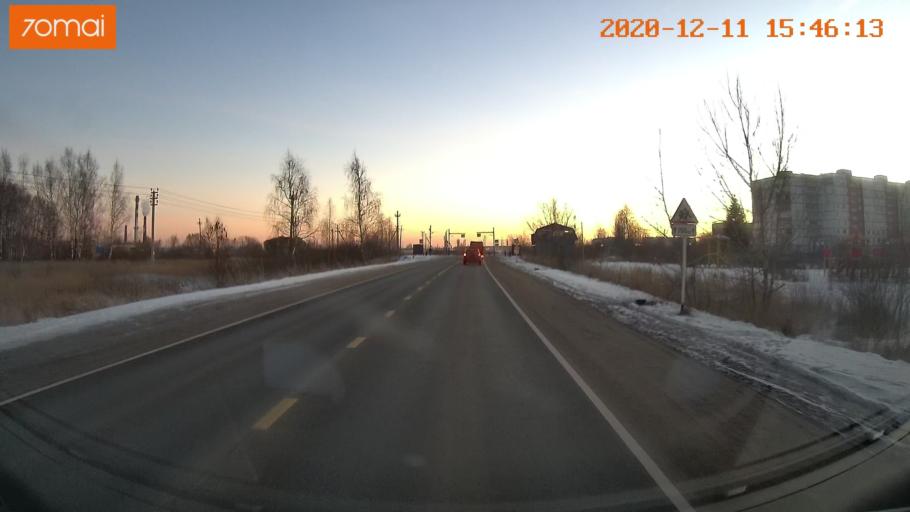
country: RU
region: Ivanovo
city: Novo-Talitsy
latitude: 57.0066
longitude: 40.8544
